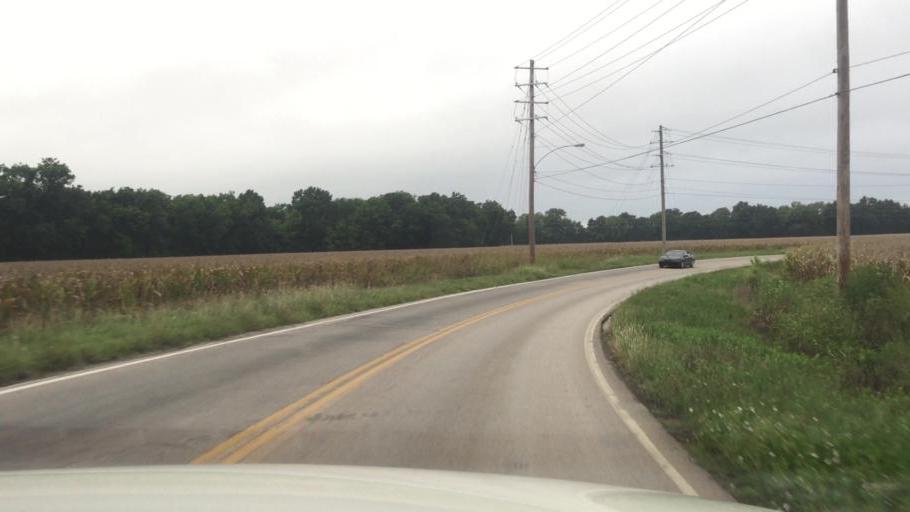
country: US
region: Kansas
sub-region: Montgomery County
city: Coffeyville
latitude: 37.0342
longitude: -95.5804
